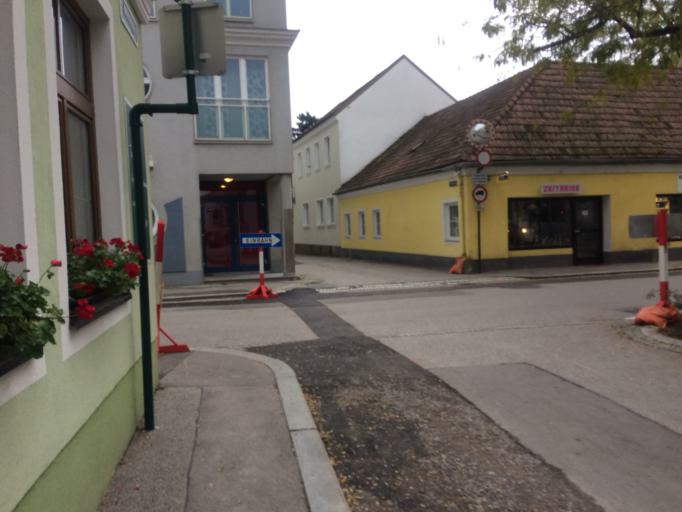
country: AT
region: Lower Austria
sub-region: Politischer Bezirk Tulln
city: Tulln
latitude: 48.3324
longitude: 16.0511
